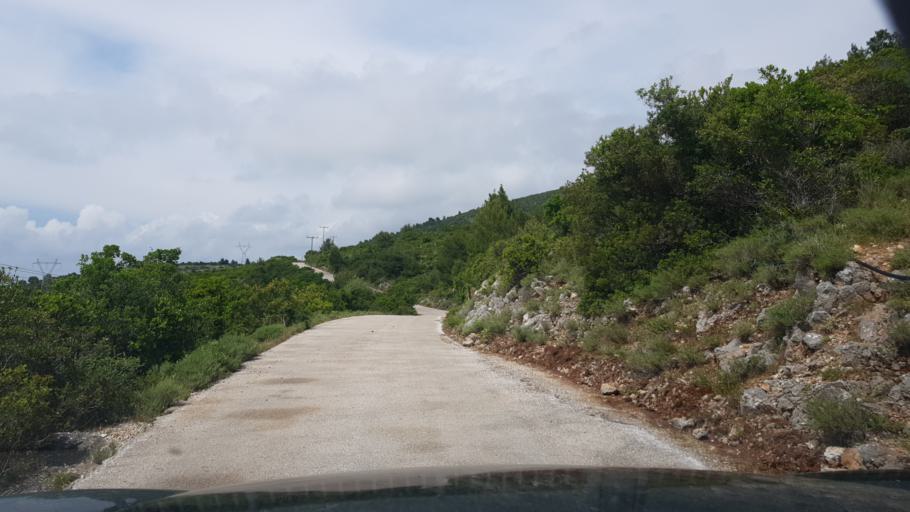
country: GR
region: Ionian Islands
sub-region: Lefkada
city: Nidri
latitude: 38.6126
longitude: 20.5646
